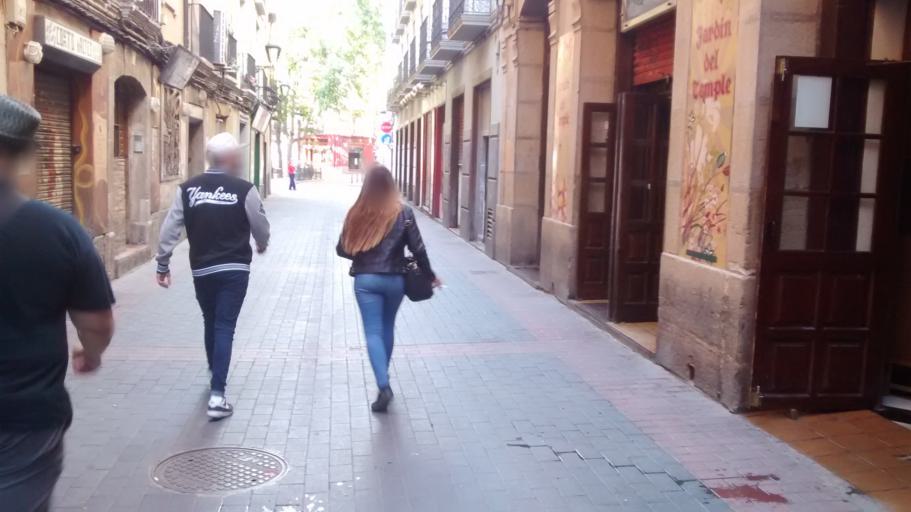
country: ES
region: Aragon
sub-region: Provincia de Zaragoza
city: Zaragoza
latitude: 41.6555
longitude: -0.8819
